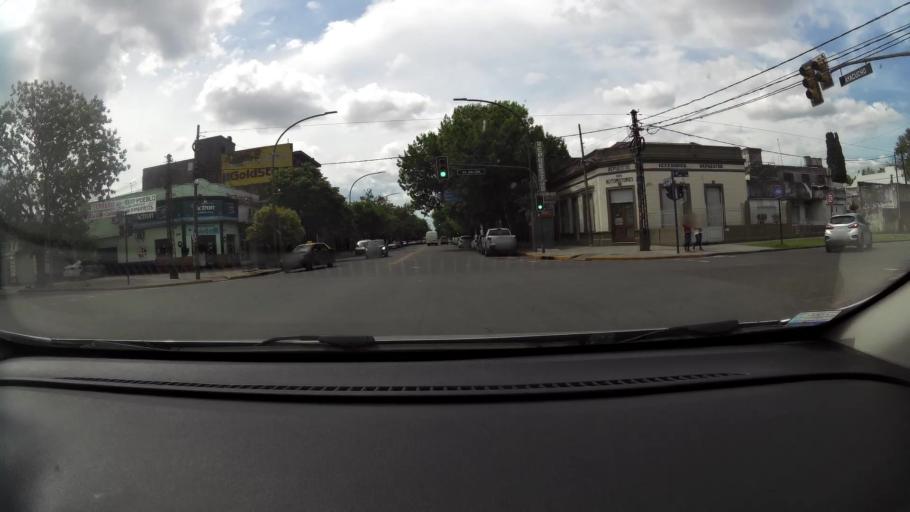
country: AR
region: Santa Fe
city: Gobernador Galvez
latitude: -33.0026
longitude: -60.6360
